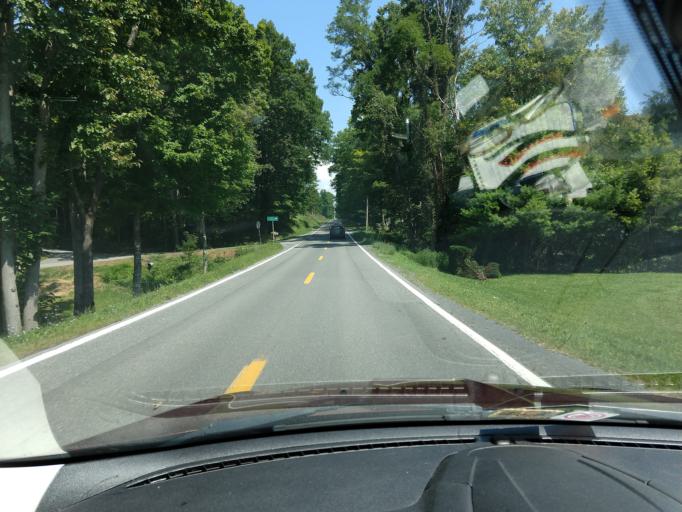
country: US
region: West Virginia
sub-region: Greenbrier County
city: Fairlea
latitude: 37.8290
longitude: -80.5578
